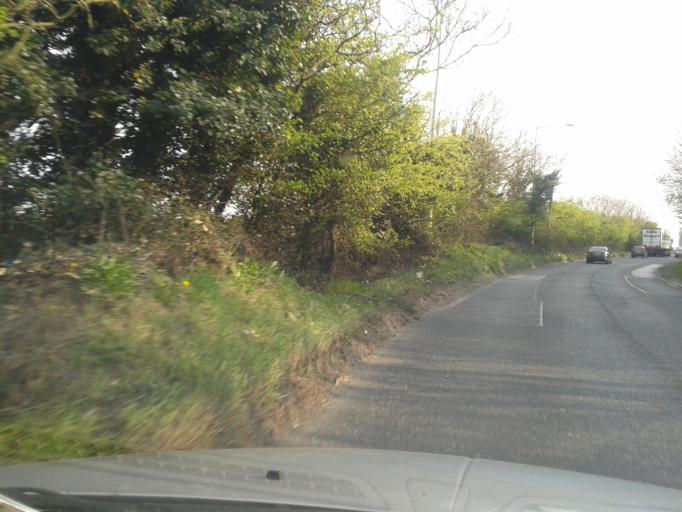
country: IE
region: Leinster
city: Ballymun
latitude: 53.4156
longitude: -6.2655
